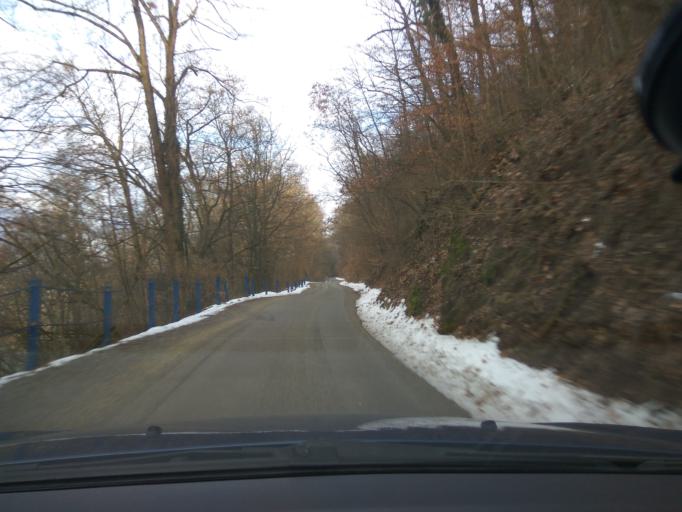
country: SK
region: Banskobystricky
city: Zarnovica
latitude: 48.4758
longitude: 18.7345
